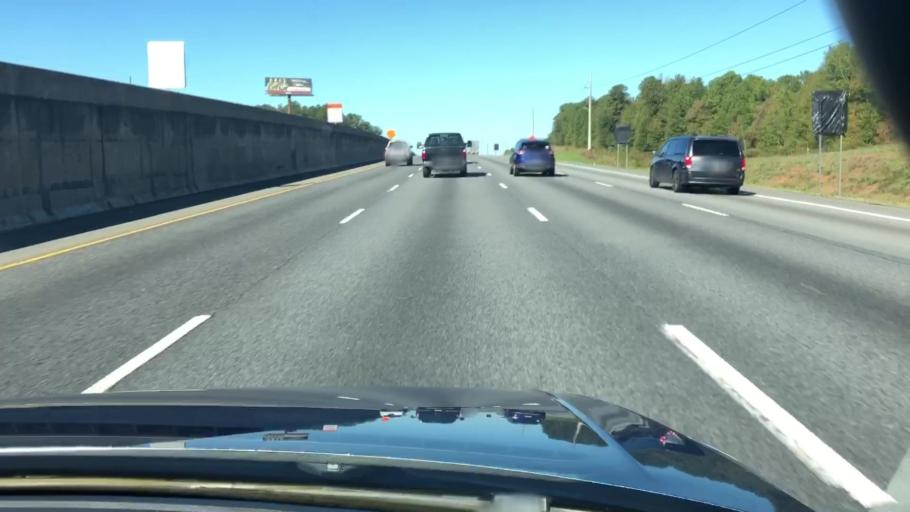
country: US
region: Georgia
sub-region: Monroe County
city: Forsyth
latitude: 33.0021
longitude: -83.8627
